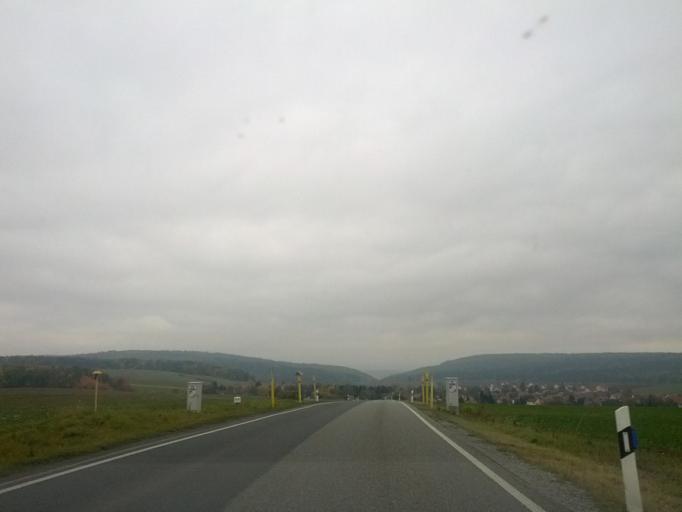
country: DE
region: Thuringia
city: Klettbach
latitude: 50.9217
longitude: 11.1449
